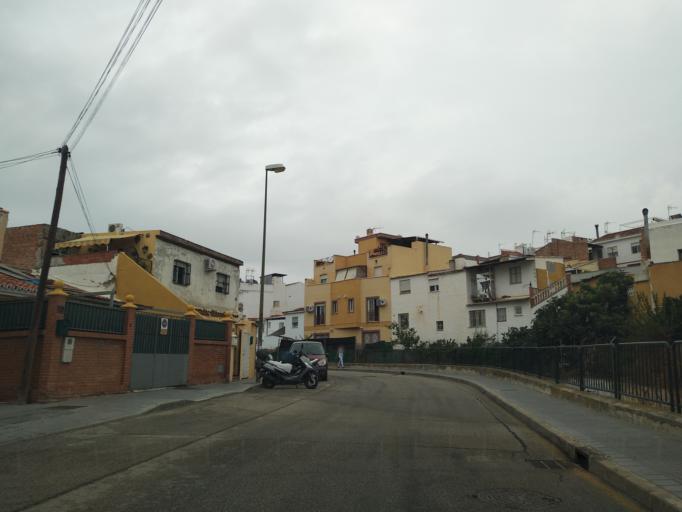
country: ES
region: Andalusia
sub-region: Provincia de Malaga
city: Malaga
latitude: 36.7411
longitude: -4.4815
